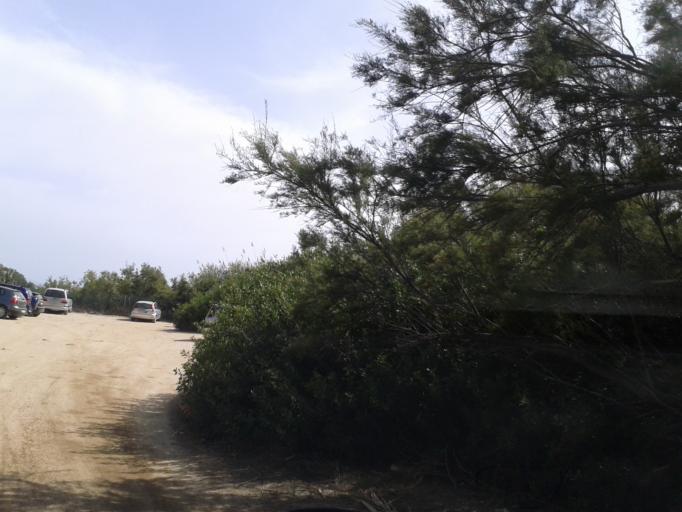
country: IT
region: Sardinia
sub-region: Provincia di Cagliari
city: Villasimius
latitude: 39.1358
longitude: 9.4888
